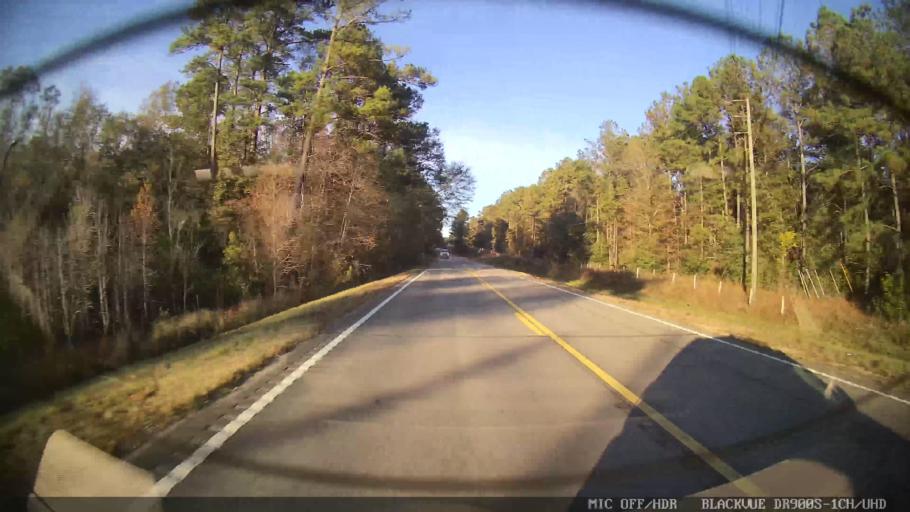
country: US
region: Mississippi
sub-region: Lamar County
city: Purvis
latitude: 31.0749
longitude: -89.4198
